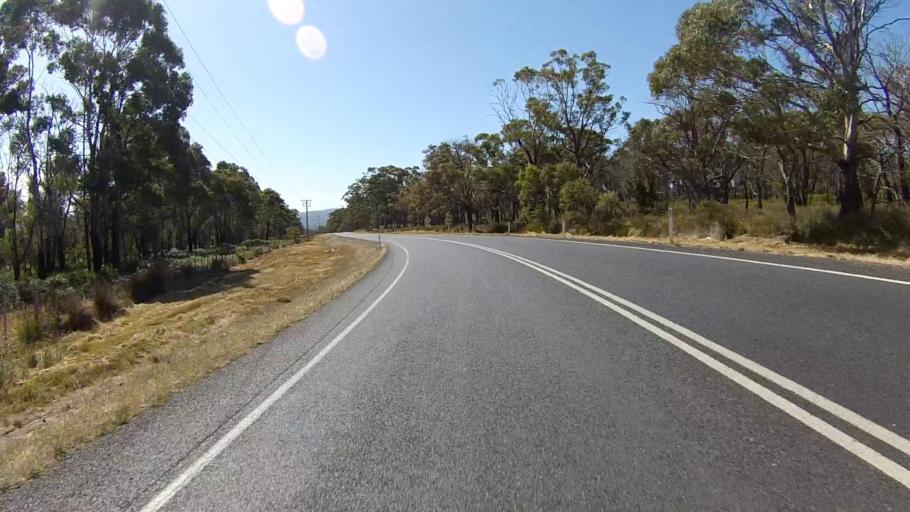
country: AU
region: Tasmania
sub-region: Sorell
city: Sorell
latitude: -42.5386
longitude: 147.8976
